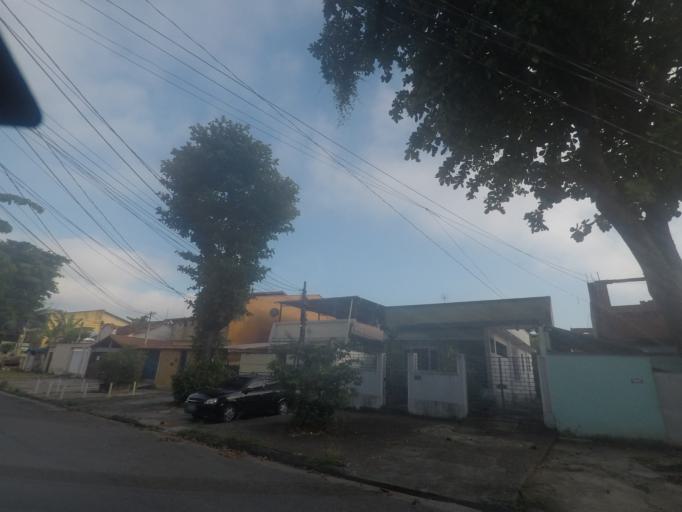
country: BR
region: Rio de Janeiro
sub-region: Duque De Caxias
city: Duque de Caxias
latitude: -22.8348
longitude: -43.2699
